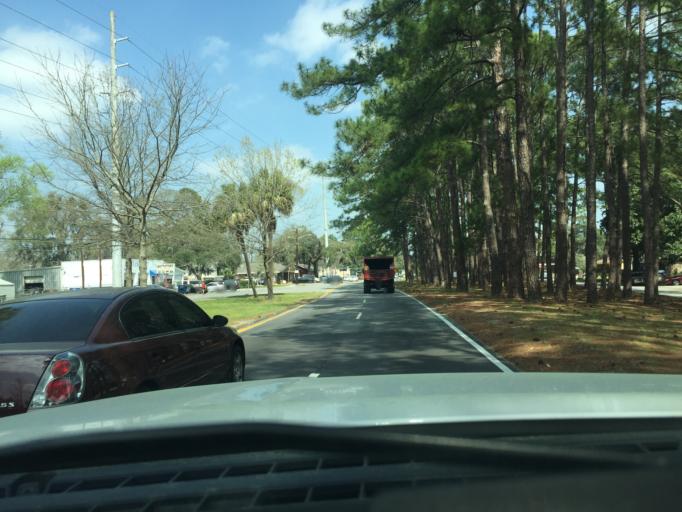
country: US
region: Georgia
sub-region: Chatham County
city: Savannah
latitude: 32.0379
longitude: -81.1119
